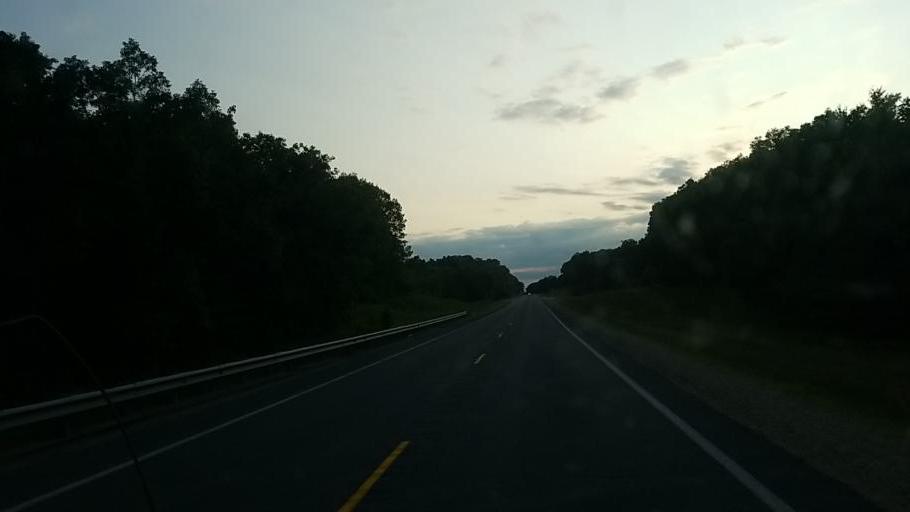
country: US
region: Michigan
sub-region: Newaygo County
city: Newaygo
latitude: 43.4056
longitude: -85.7094
